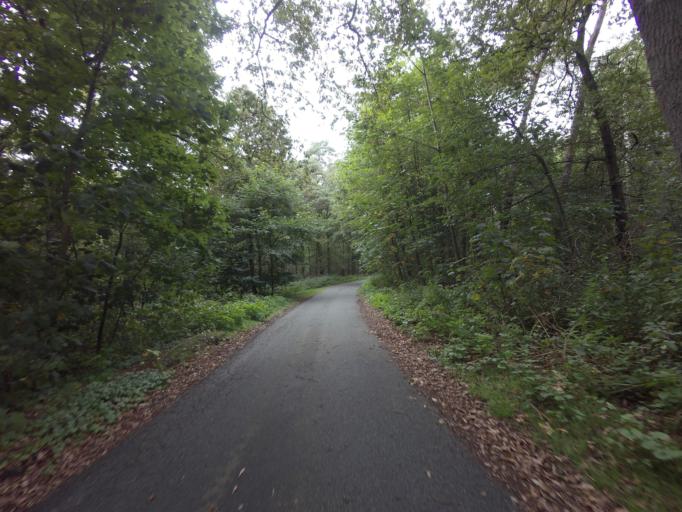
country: NL
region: Overijssel
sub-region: Gemeente Losser
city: Losser
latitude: 52.2637
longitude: 7.0466
